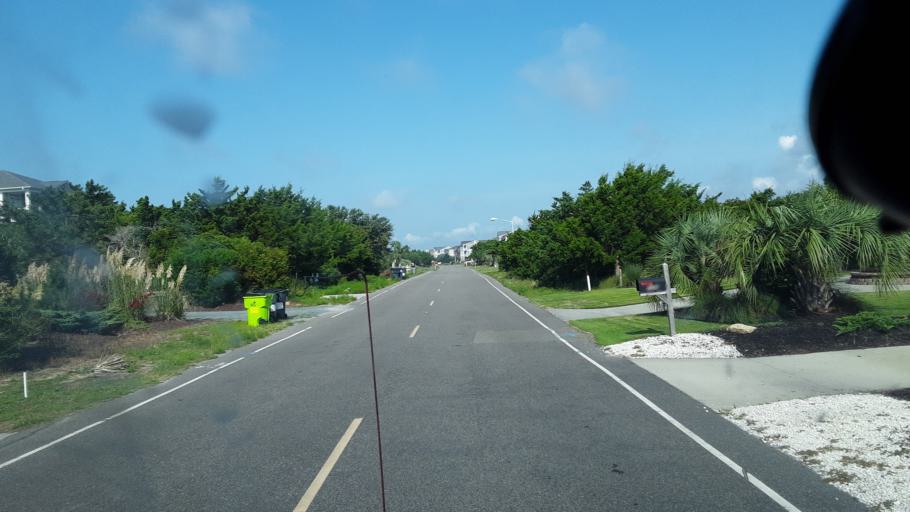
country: US
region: North Carolina
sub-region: Brunswick County
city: Southport
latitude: 33.8952
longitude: -78.0452
